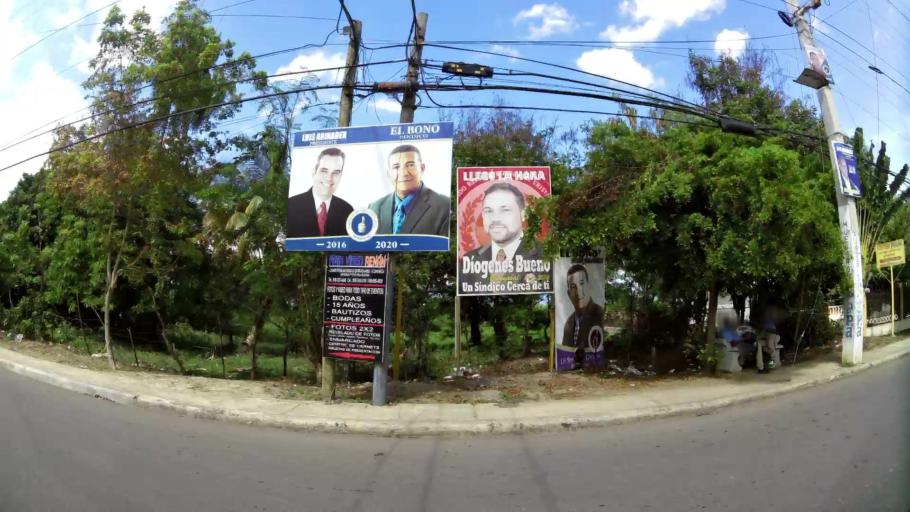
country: DO
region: Santiago
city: Licey al Medio
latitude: 19.3863
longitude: -70.6299
